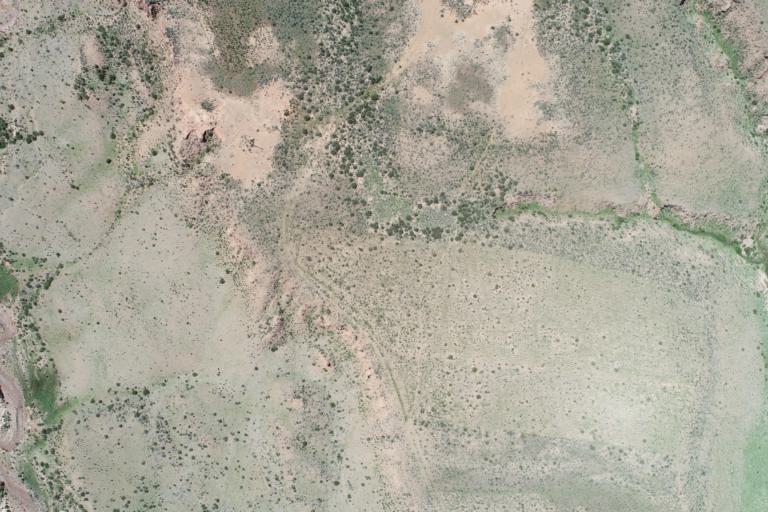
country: BO
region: La Paz
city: Curahuara de Carangas
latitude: -17.3227
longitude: -68.5080
